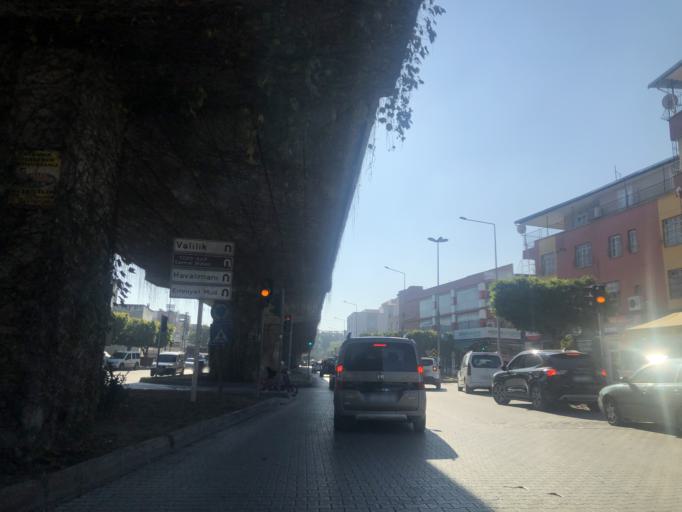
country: TR
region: Adana
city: Seyhan
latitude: 36.9827
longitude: 35.3205
